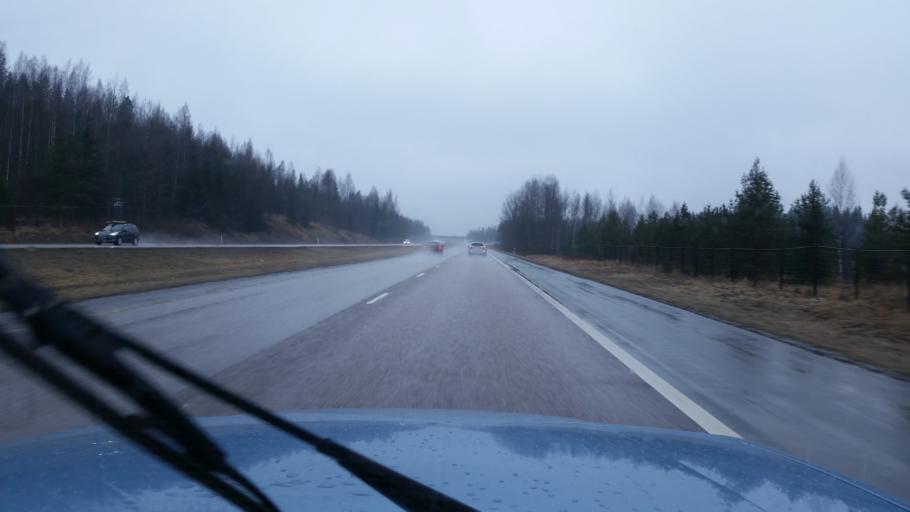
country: FI
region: Uusimaa
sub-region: Helsinki
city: Hyvinge
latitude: 60.6531
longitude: 24.8013
